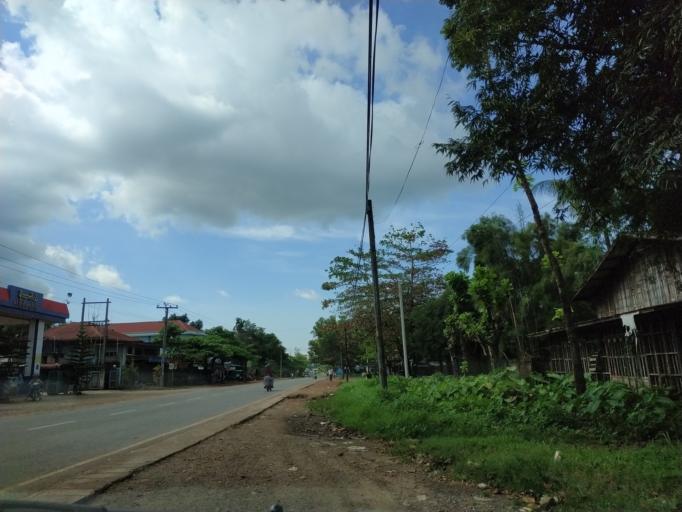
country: MM
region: Mon
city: Kyaikkami
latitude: 15.9520
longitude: 97.7305
